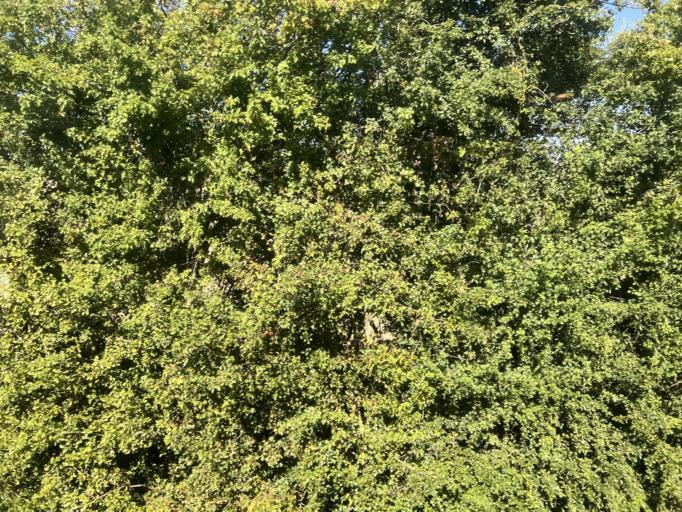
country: GB
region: England
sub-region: Lincolnshire
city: Spilsby
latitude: 53.0697
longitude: 0.0710
